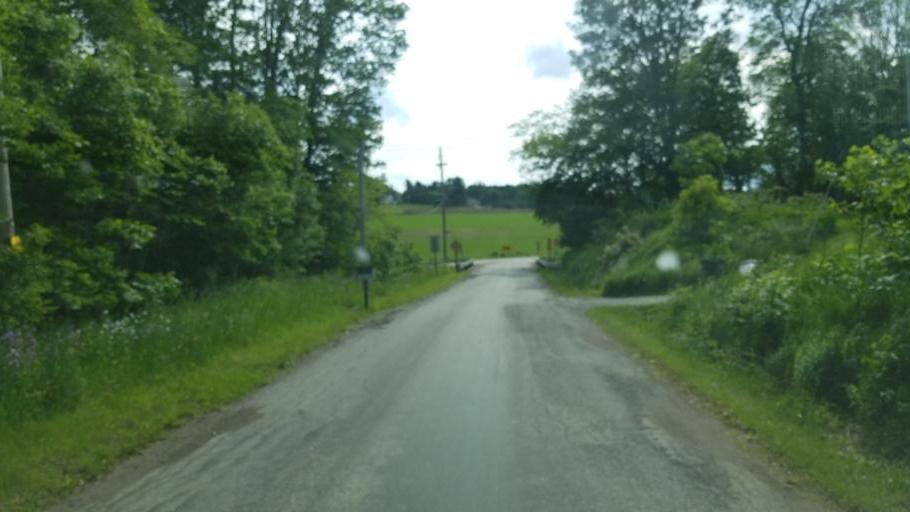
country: US
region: Ohio
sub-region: Richland County
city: Lincoln Heights
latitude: 40.8475
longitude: -82.5075
